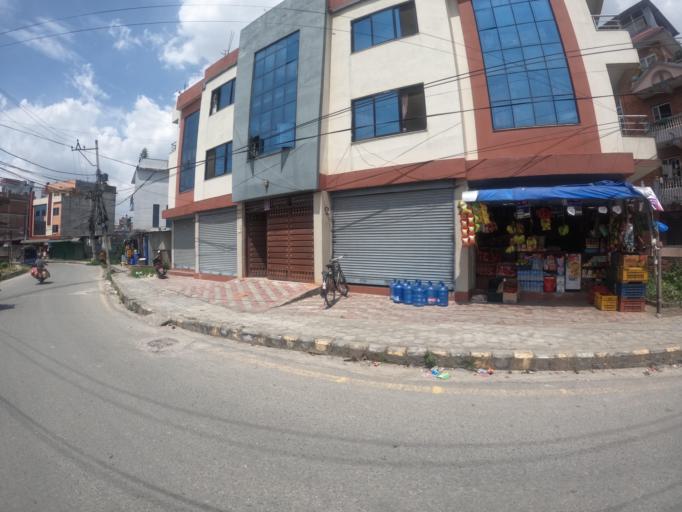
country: NP
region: Central Region
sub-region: Bagmati Zone
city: Bhaktapur
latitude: 27.6750
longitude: 85.3814
